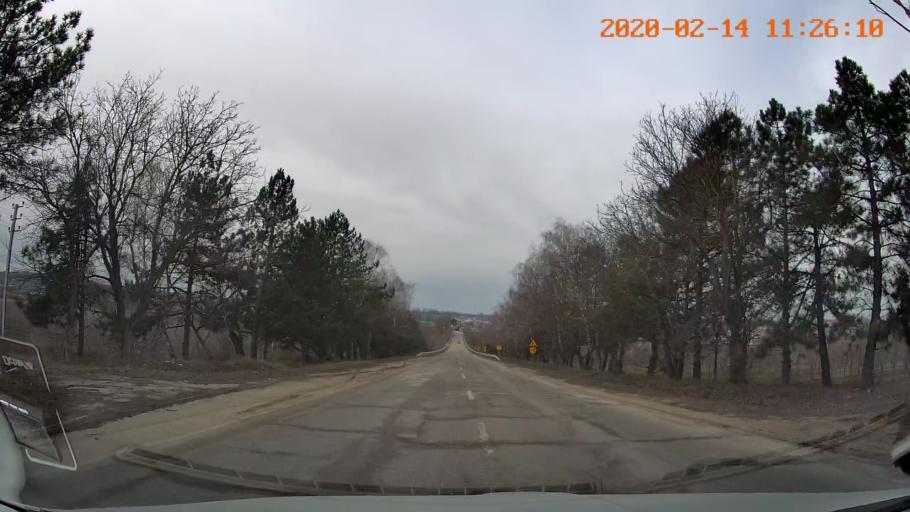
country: MD
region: Briceni
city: Briceni
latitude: 48.3518
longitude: 27.0944
